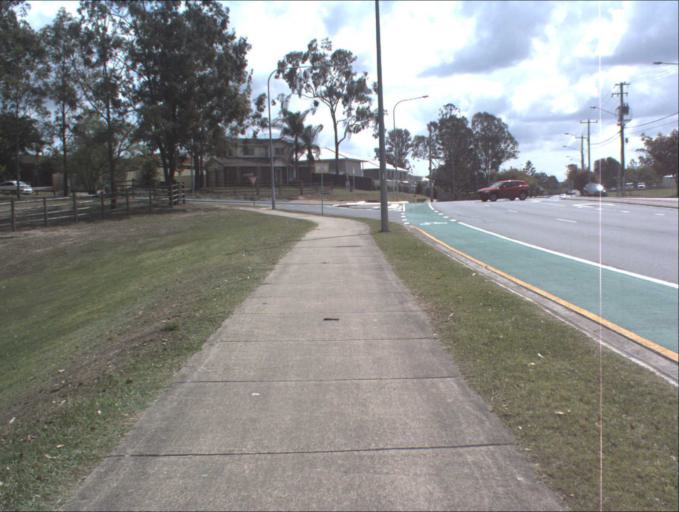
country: AU
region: Queensland
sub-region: Logan
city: Waterford West
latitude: -27.6831
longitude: 153.1371
